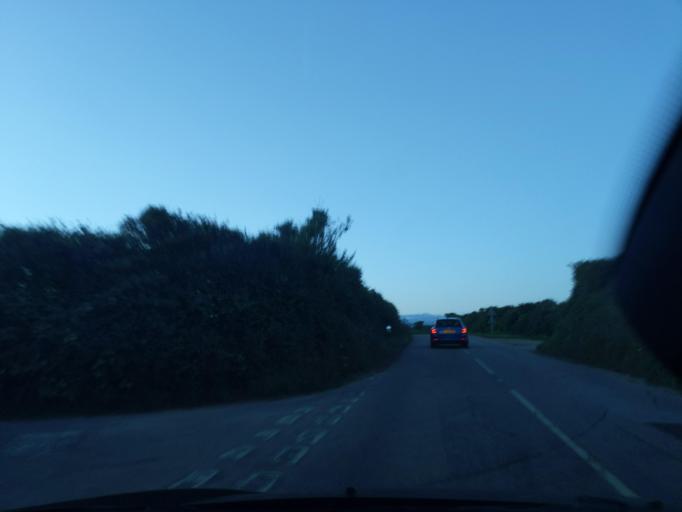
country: GB
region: England
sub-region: Cornwall
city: St. Buryan
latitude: 50.0669
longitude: -5.6333
